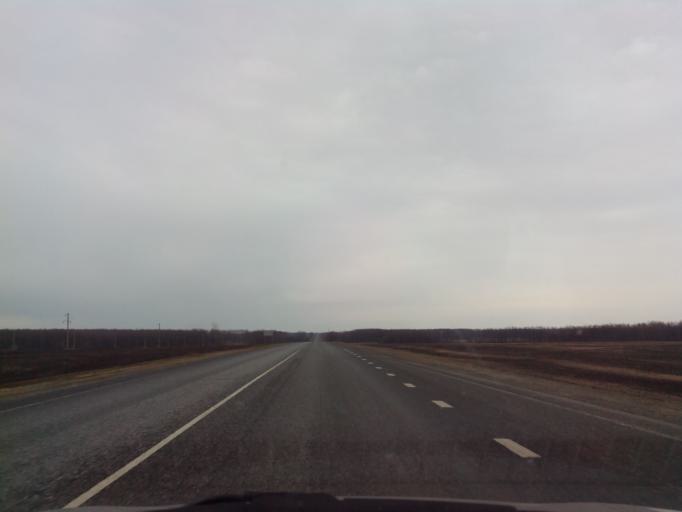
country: RU
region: Tambov
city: Zavoronezhskoye
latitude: 52.9906
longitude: 40.5557
